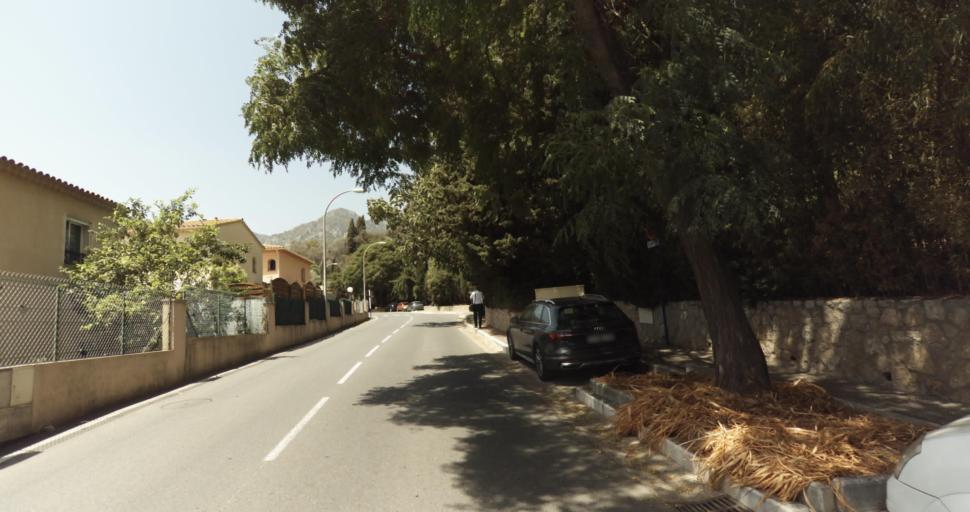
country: FR
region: Provence-Alpes-Cote d'Azur
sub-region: Departement des Alpes-Maritimes
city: Roquebrune-Cap-Martin
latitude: 43.7745
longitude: 7.4753
